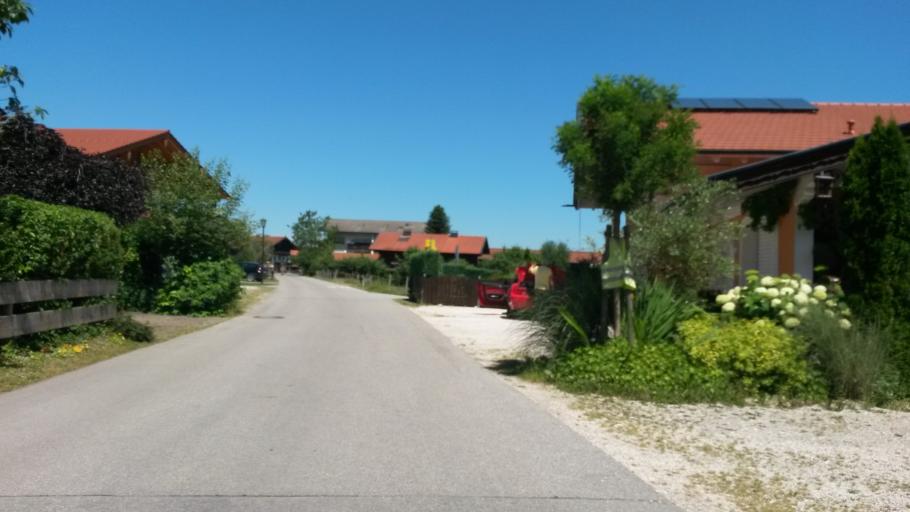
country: DE
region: Bavaria
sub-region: Upper Bavaria
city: Grassau
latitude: 47.7921
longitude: 12.4180
